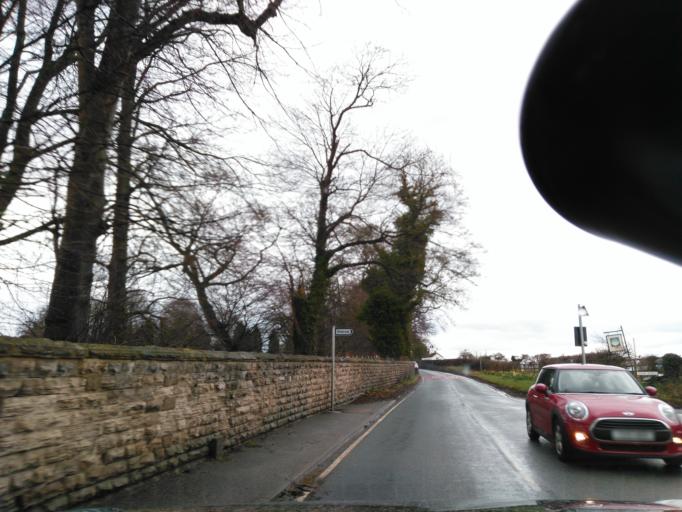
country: GB
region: England
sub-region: North Yorkshire
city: Ripon
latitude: 54.1425
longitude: -1.4966
